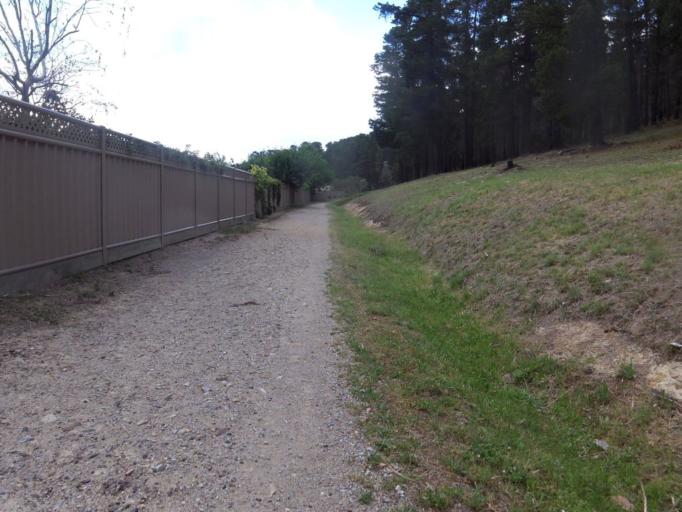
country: AU
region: Australian Capital Territory
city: Macarthur
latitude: -35.3685
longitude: 149.1162
